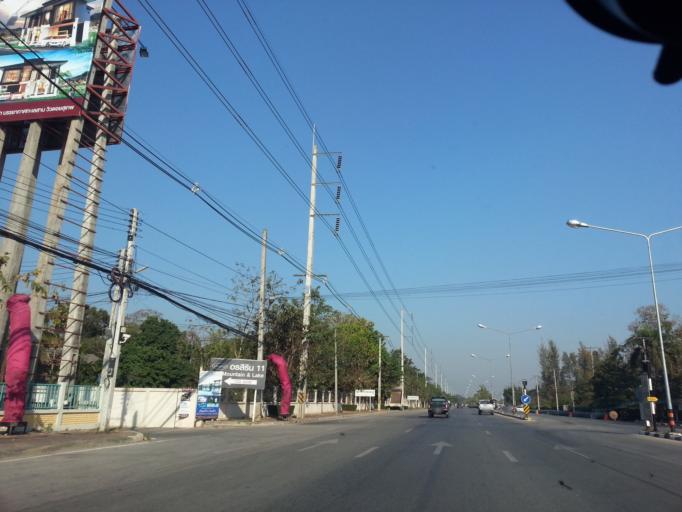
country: TH
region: Chiang Mai
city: San Sai
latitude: 18.9040
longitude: 99.0041
